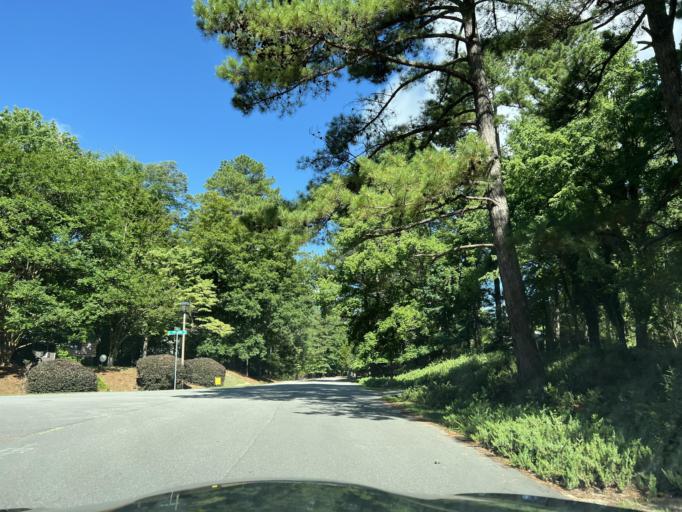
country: US
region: North Carolina
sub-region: Wake County
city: Wake Forest
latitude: 35.9411
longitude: -78.6390
